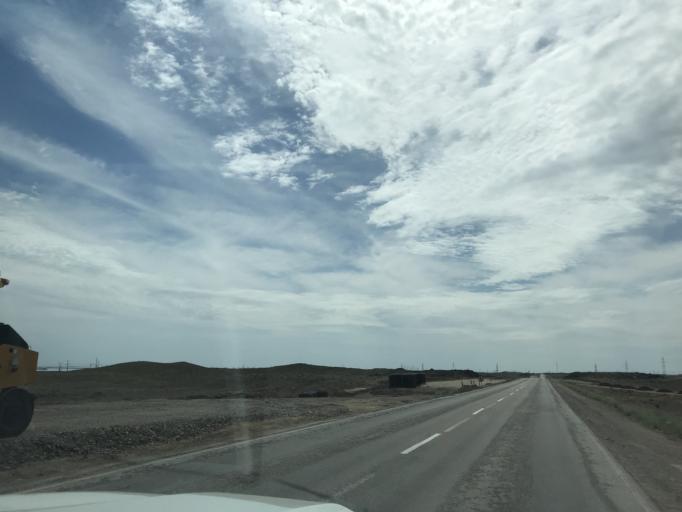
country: KZ
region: Almaty Oblysy
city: Ulken
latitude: 45.2227
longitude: 73.8565
